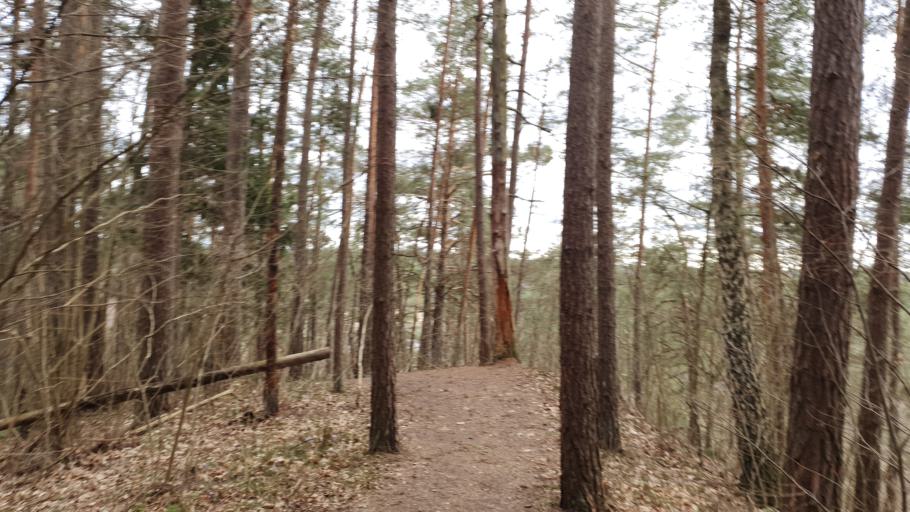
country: LT
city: Grigiskes
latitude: 54.7380
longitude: 25.0250
